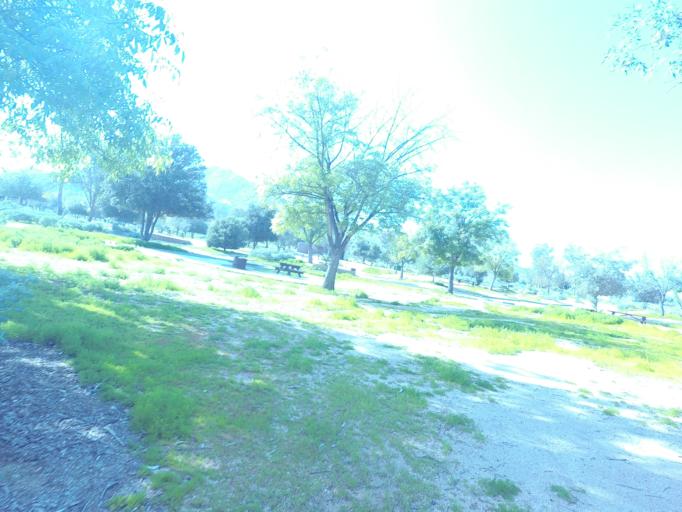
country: US
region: California
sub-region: Riverside County
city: Lakeview
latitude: 33.8749
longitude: -117.1760
